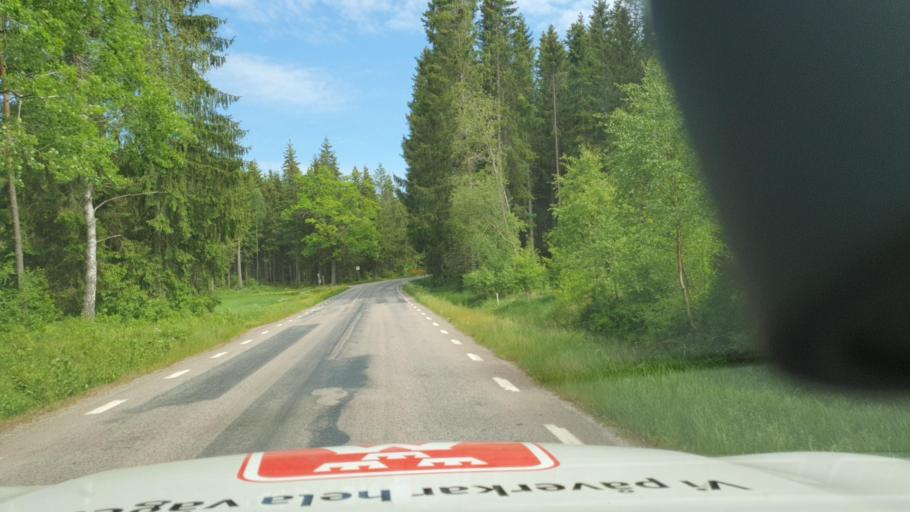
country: SE
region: Vaestra Goetaland
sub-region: Alingsas Kommun
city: Sollebrunn
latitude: 58.2120
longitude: 12.5406
